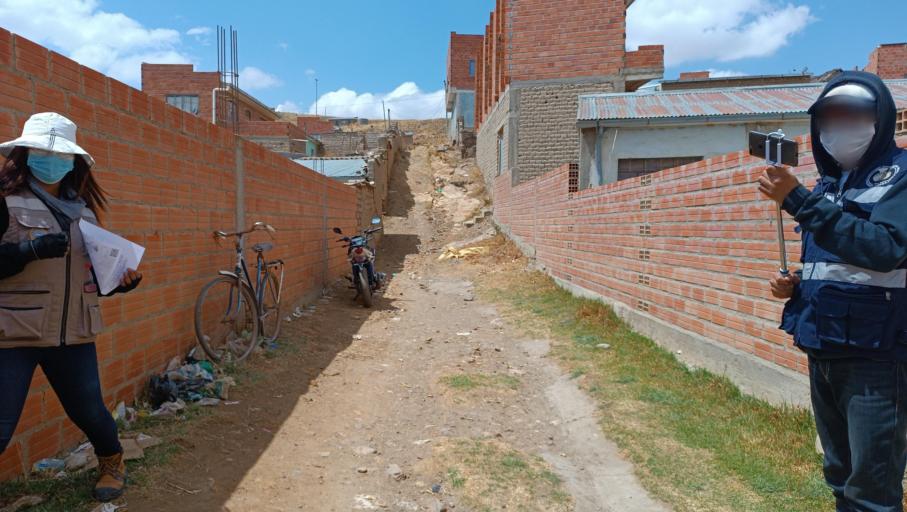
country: BO
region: La Paz
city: Batallas
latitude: -16.3850
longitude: -68.5969
